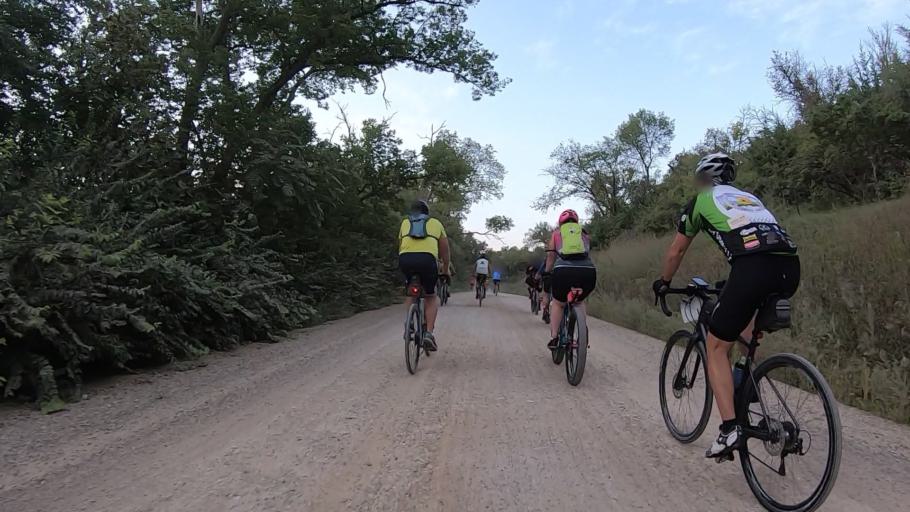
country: US
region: Kansas
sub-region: Marshall County
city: Marysville
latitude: 39.8341
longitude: -96.6653
